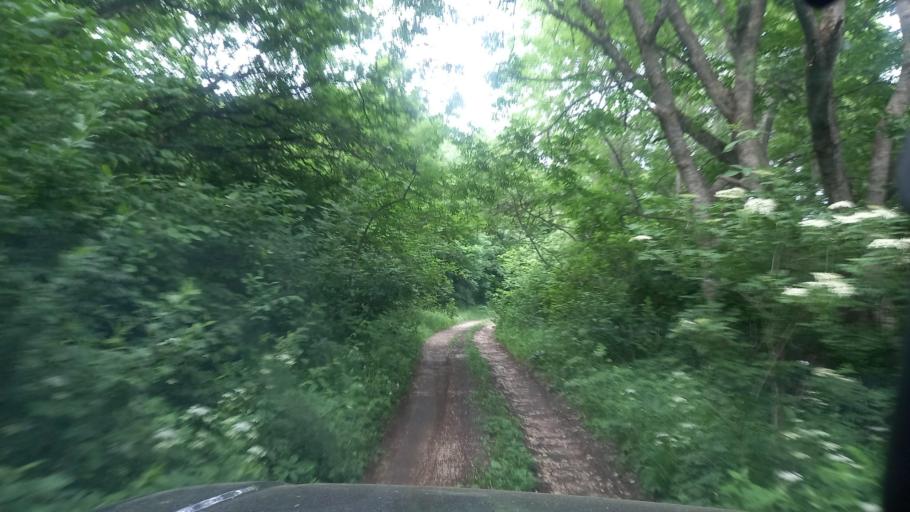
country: RU
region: Karachayevo-Cherkesiya
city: Pregradnaya
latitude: 44.0236
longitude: 41.2955
